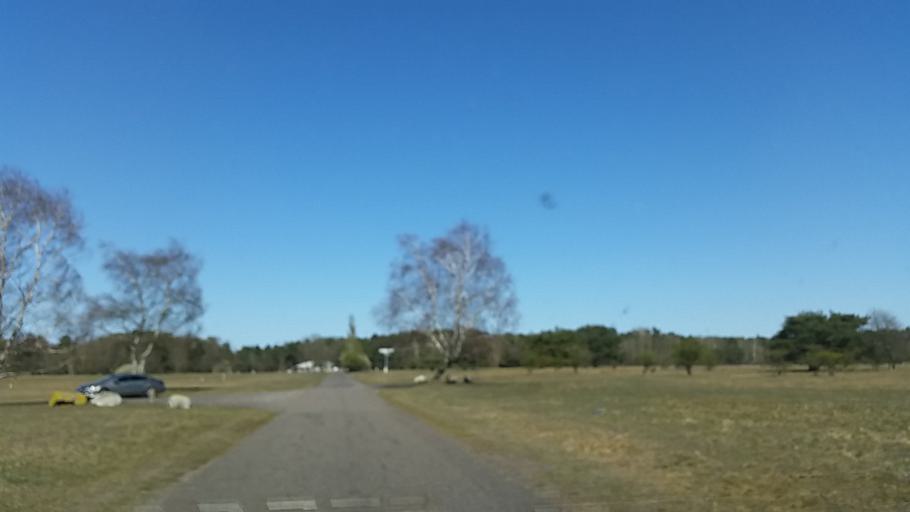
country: DE
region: Lower Saxony
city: Schneverdingen
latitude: 53.1501
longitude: 9.8275
